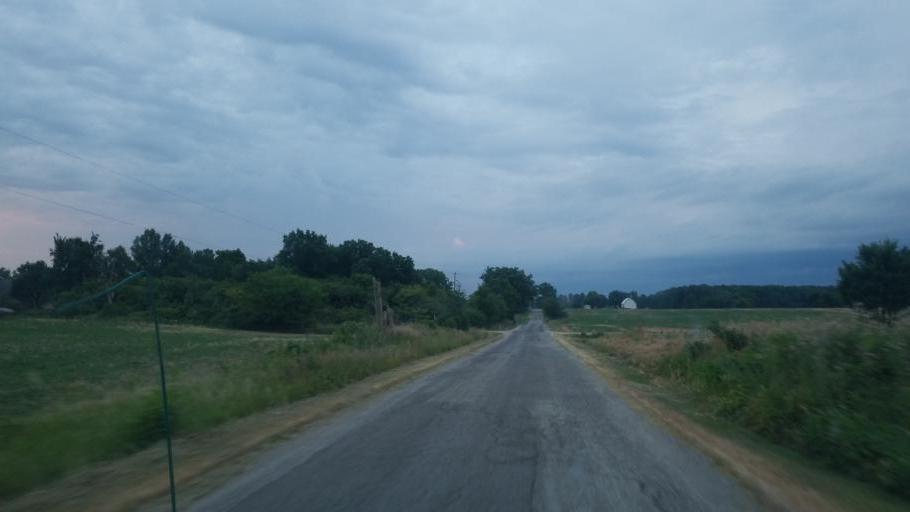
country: US
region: Ohio
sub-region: Defiance County
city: Hicksville
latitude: 41.3295
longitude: -84.8301
